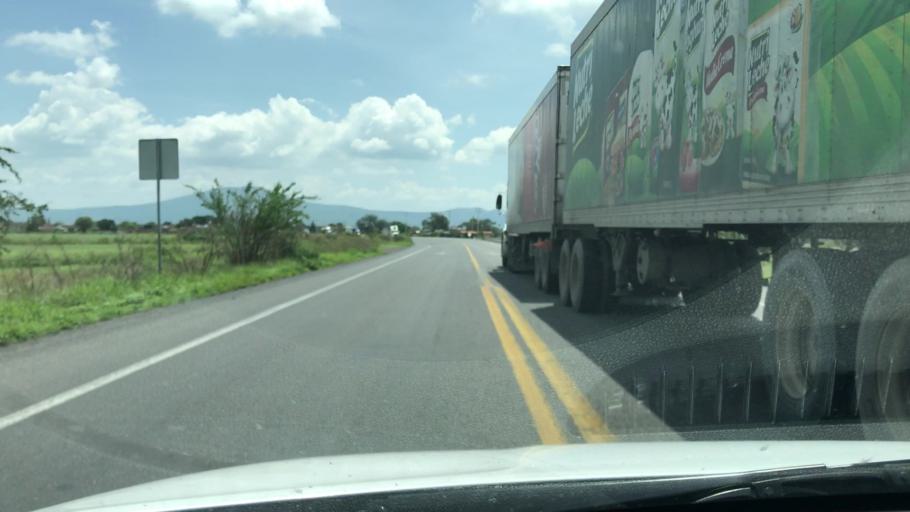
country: MX
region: Michoacan
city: Tanhuato de Guerrero
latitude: 20.2841
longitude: -102.3417
